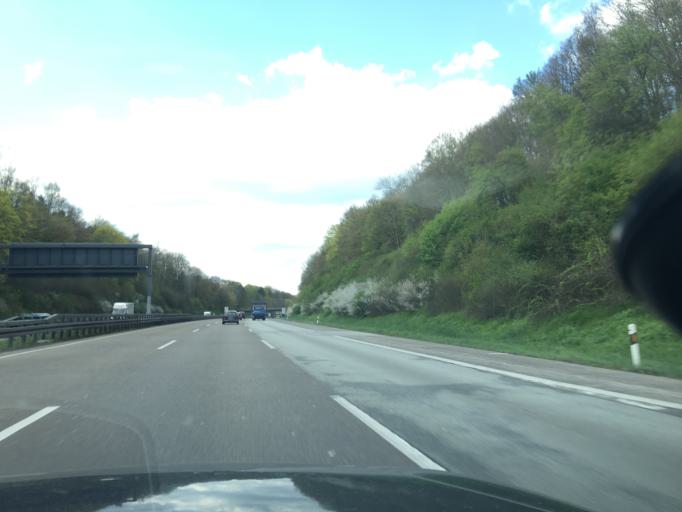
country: DE
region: Hesse
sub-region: Regierungsbezirk Giessen
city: Langgons
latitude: 50.4845
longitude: 8.6930
